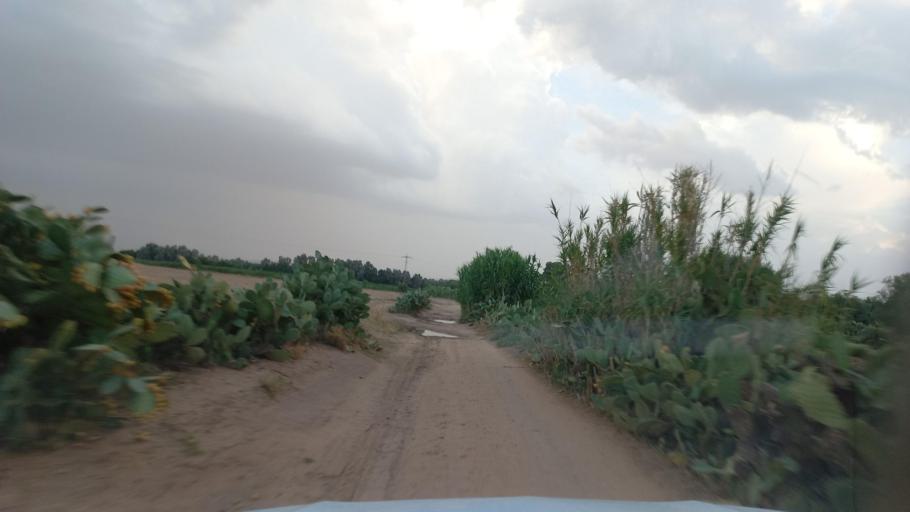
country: TN
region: Al Qasrayn
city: Kasserine
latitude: 35.2754
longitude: 9.0584
